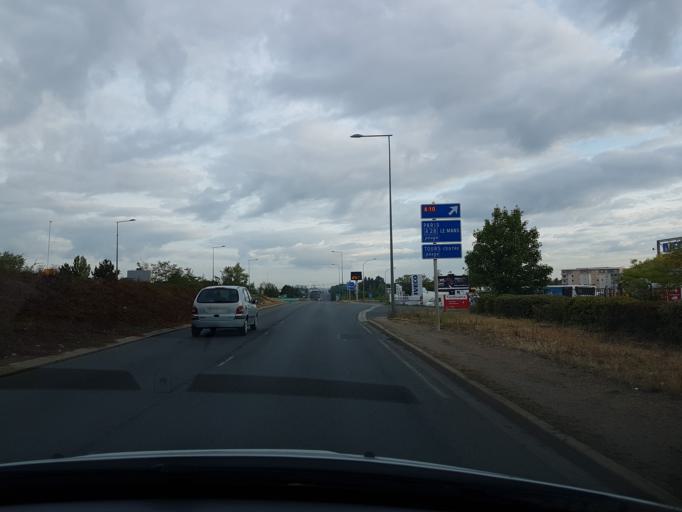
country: FR
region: Centre
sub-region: Departement d'Indre-et-Loire
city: Chambray-les-Tours
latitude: 47.3447
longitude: 0.7024
